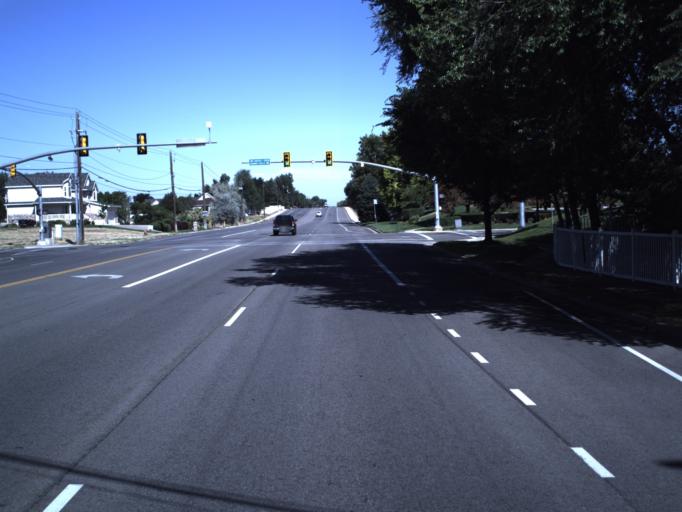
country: US
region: Utah
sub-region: Davis County
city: Fruit Heights
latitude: 41.0157
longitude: -111.9175
